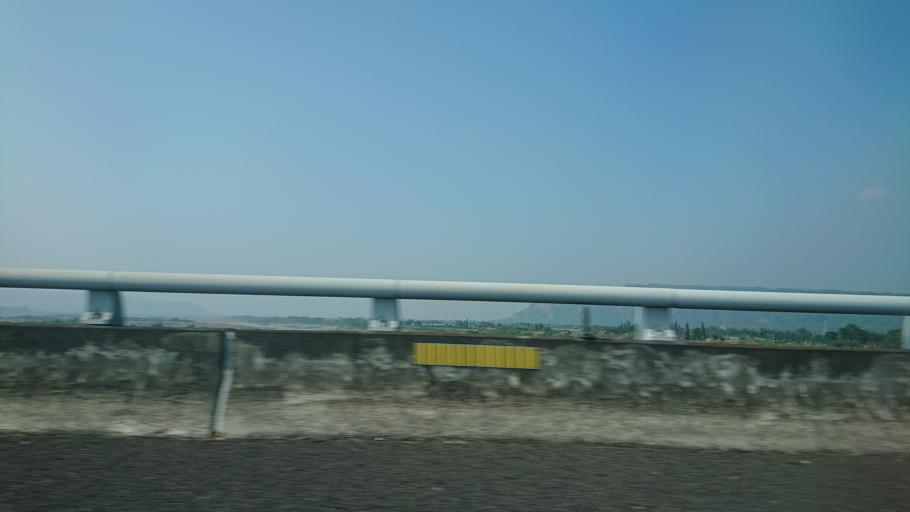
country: TW
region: Taiwan
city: Lugu
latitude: 23.8056
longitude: 120.6974
